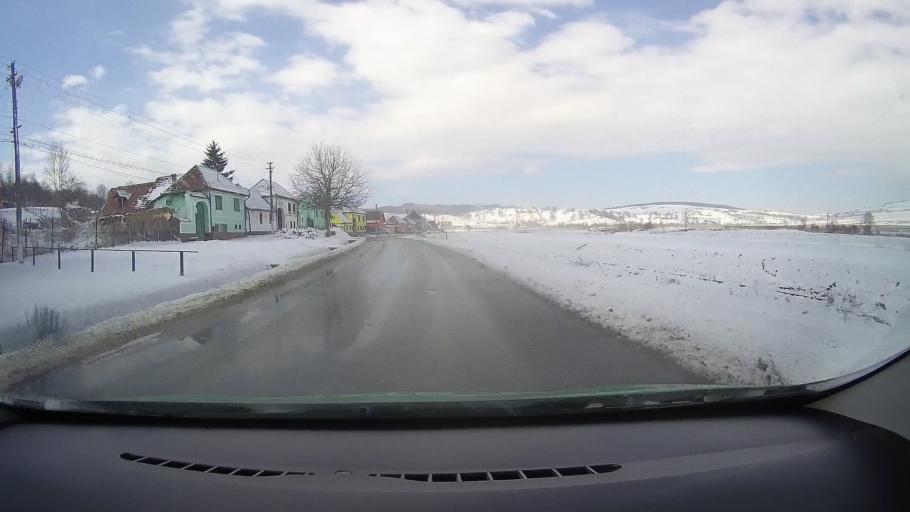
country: RO
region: Sibiu
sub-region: Comuna Altina
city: Altina
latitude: 45.9361
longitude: 24.4615
